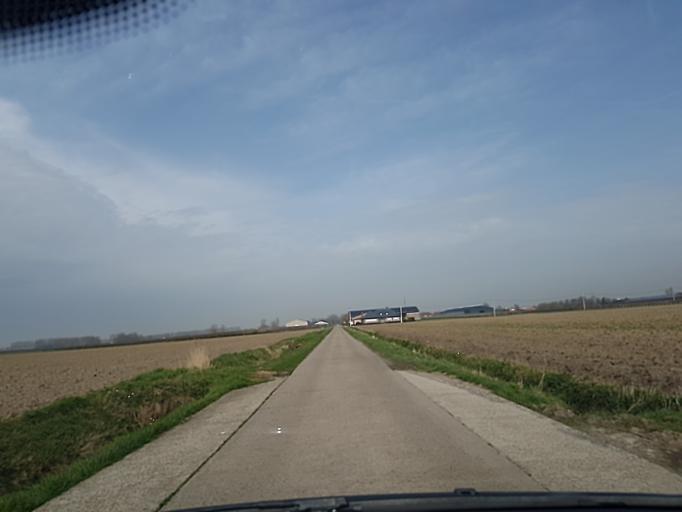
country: BE
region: Flanders
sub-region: Provincie Oost-Vlaanderen
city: Sint-Gillis-Waas
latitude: 51.2702
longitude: 4.1779
